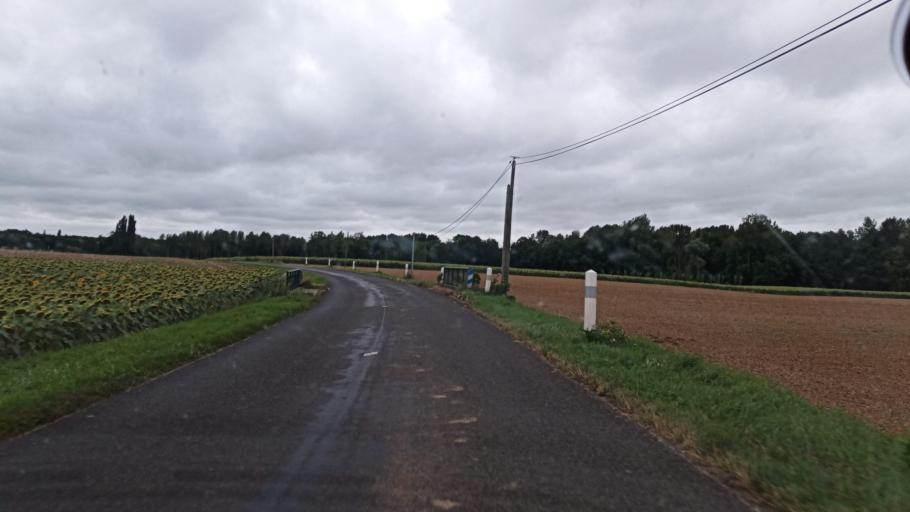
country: FR
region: Bourgogne
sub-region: Departement de l'Yonne
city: Cheroy
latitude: 48.2528
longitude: 3.0273
